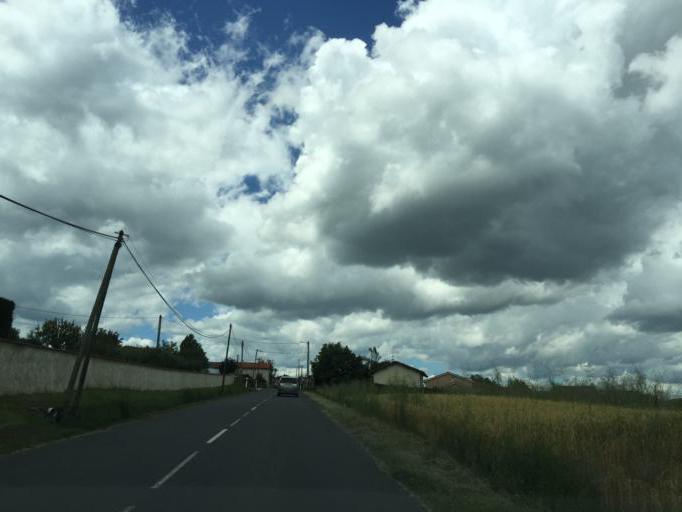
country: FR
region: Rhone-Alpes
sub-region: Departement de la Loire
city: Saint-Marcellin-en-Forez
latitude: 45.5043
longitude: 4.1395
